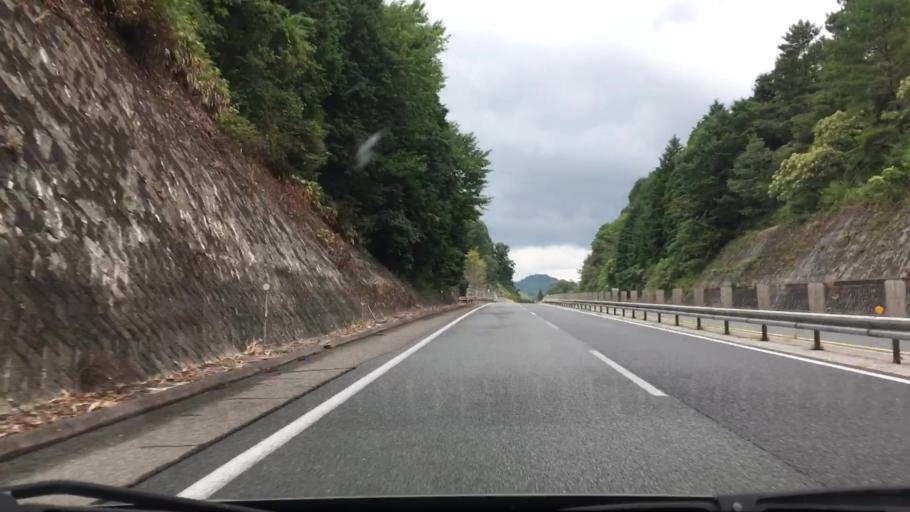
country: JP
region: Okayama
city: Niimi
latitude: 34.9370
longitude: 133.3280
